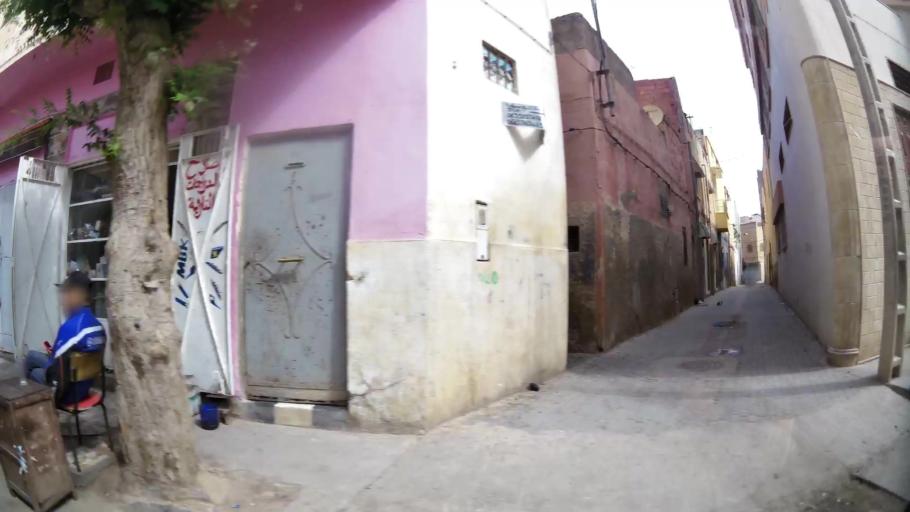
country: MA
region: Oriental
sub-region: Oujda-Angad
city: Oujda
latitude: 34.6832
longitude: -1.9124
